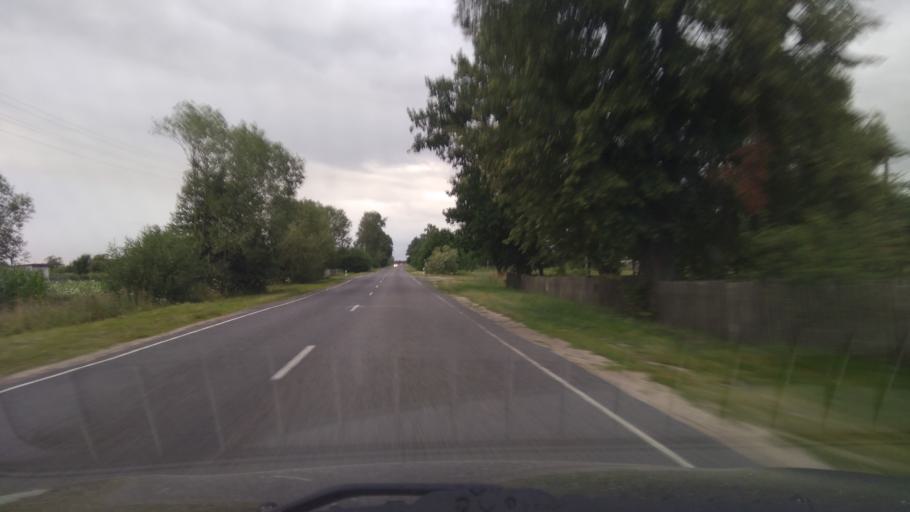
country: BY
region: Brest
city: Byaroza
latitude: 52.4237
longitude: 24.9812
